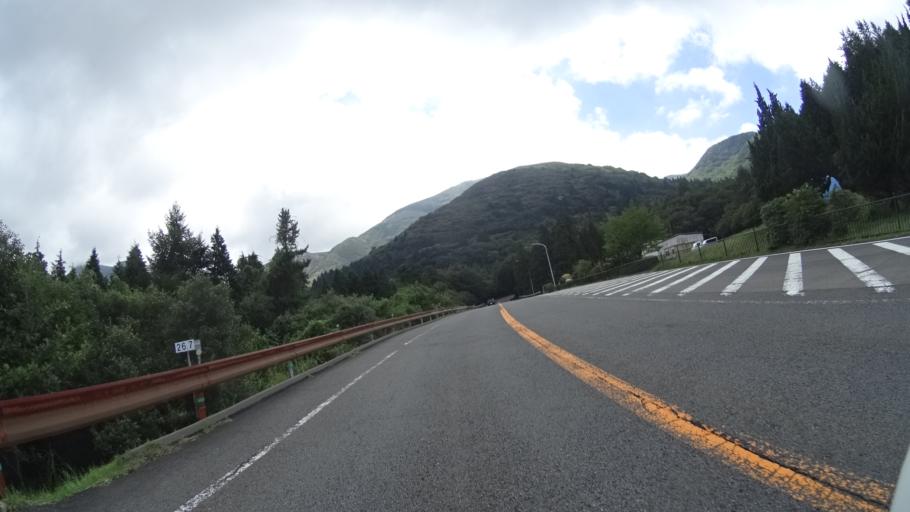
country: JP
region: Oita
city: Tsukawaki
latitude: 33.1038
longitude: 131.2214
